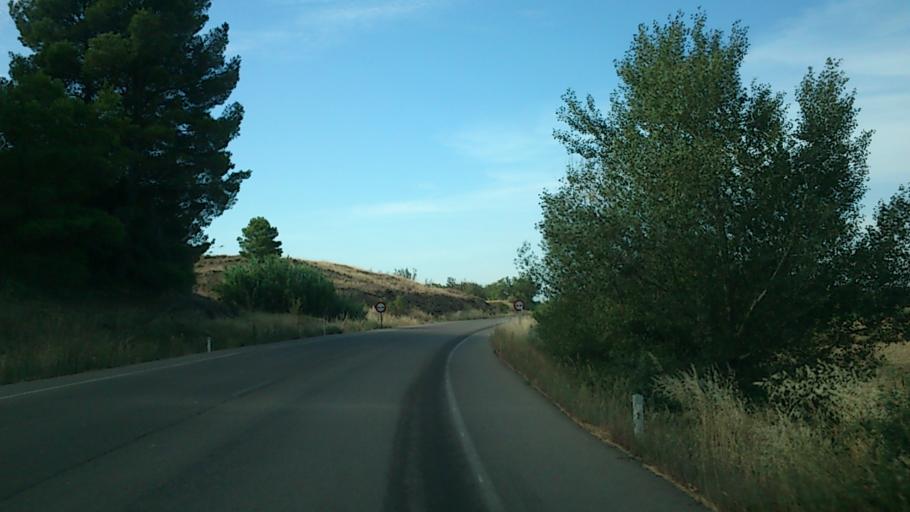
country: ES
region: Aragon
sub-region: Provincia de Zaragoza
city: Villanueva de Gallego
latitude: 41.7817
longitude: -0.7878
